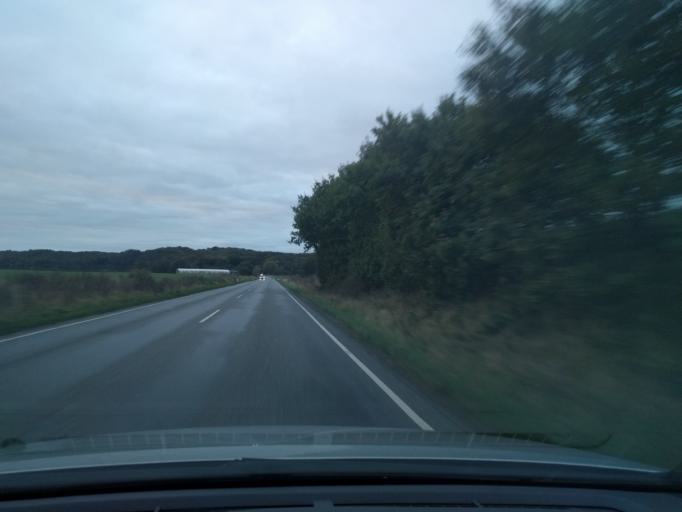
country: DK
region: South Denmark
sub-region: Odense Kommune
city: Bellinge
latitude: 55.2192
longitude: 10.3029
